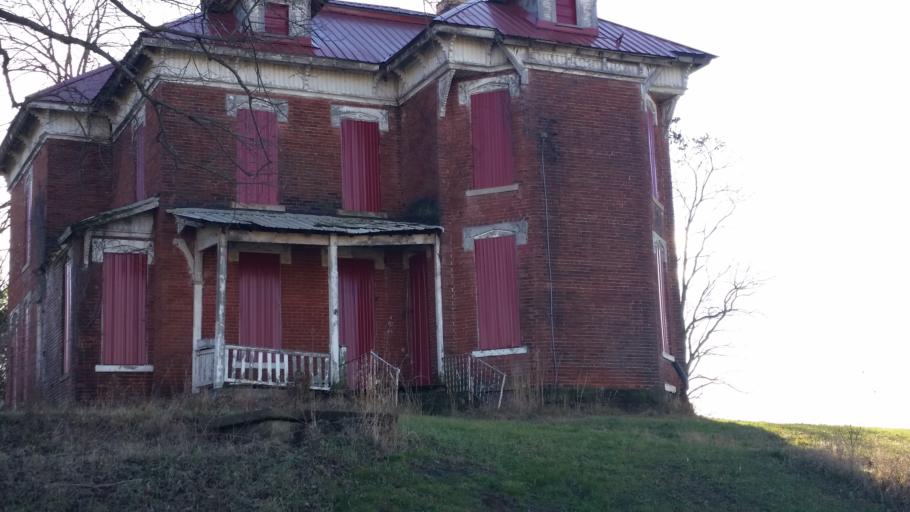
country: US
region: Ohio
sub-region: Carroll County
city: Carrollton
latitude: 40.6181
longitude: -81.0008
